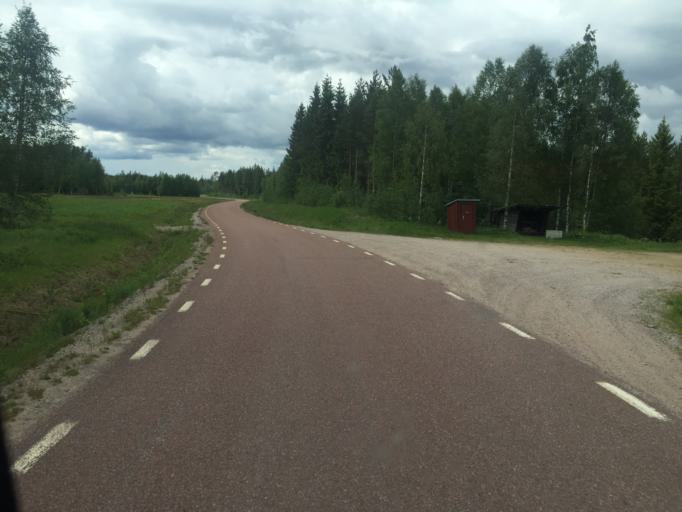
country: SE
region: Dalarna
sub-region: Vansbro Kommun
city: Vansbro
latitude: 60.4719
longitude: 13.9420
